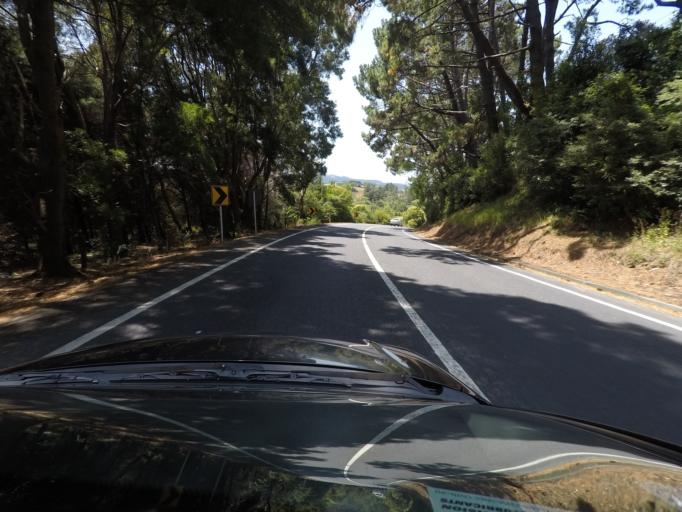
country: NZ
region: Auckland
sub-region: Auckland
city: Warkworth
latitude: -36.3469
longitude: 174.7252
